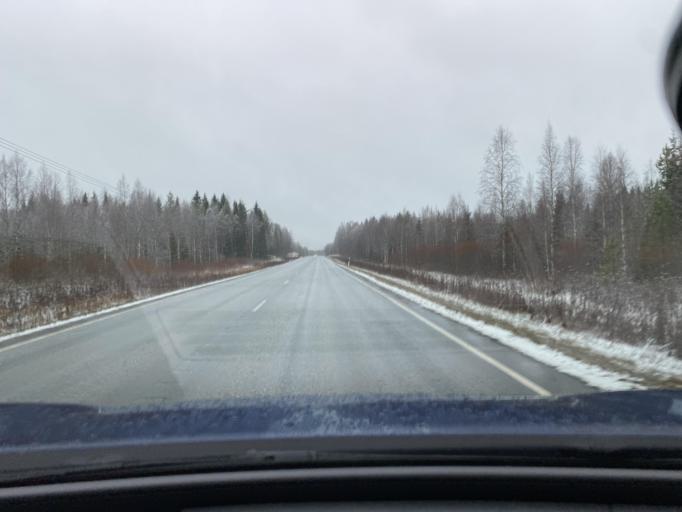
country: FI
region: Northern Ostrobothnia
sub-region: Oulu
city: Kiiminki
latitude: 65.1343
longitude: 25.8159
